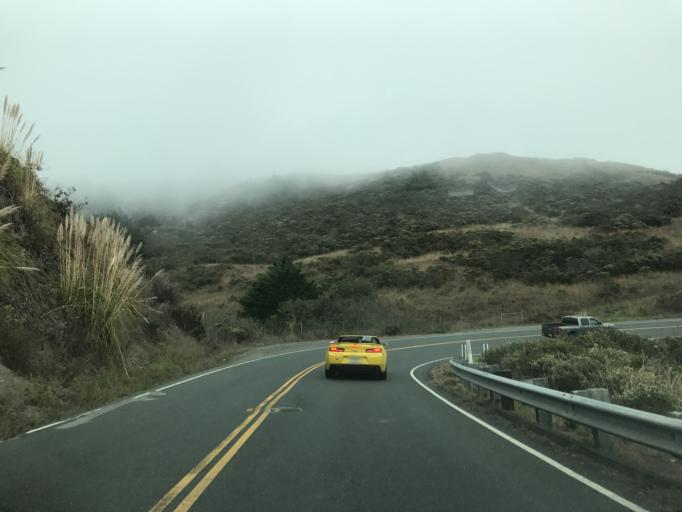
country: US
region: California
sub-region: Sonoma County
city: Monte Rio
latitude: 38.4594
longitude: -123.1361
